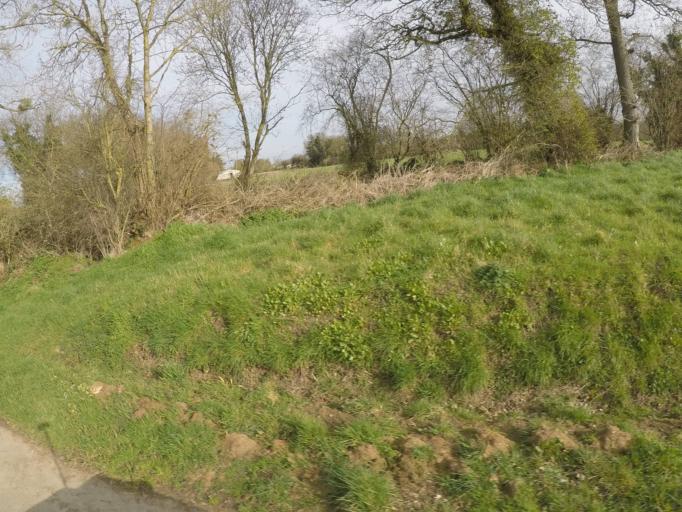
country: FR
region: Brittany
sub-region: Departement des Cotes-d'Armor
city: Plelo
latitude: 48.5244
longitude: -2.9574
